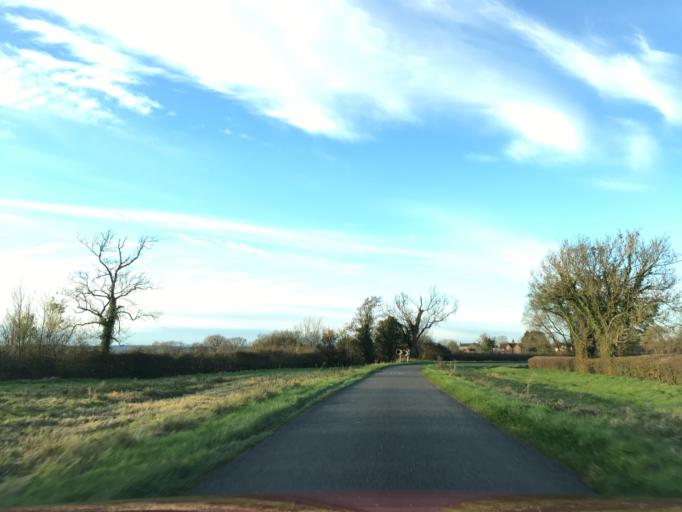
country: GB
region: England
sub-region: South Gloucestershire
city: Hill
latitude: 51.6502
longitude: -2.5174
